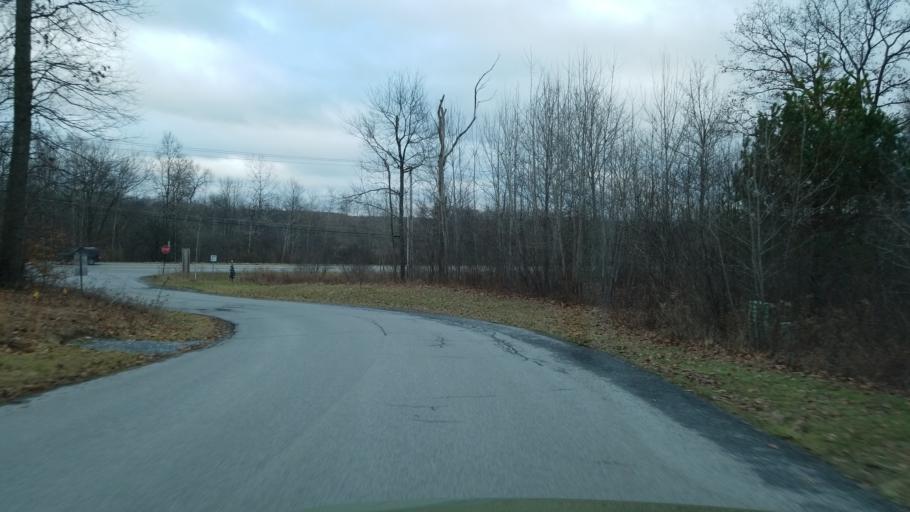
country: US
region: Pennsylvania
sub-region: Jefferson County
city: Falls Creek
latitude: 41.1359
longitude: -78.8081
